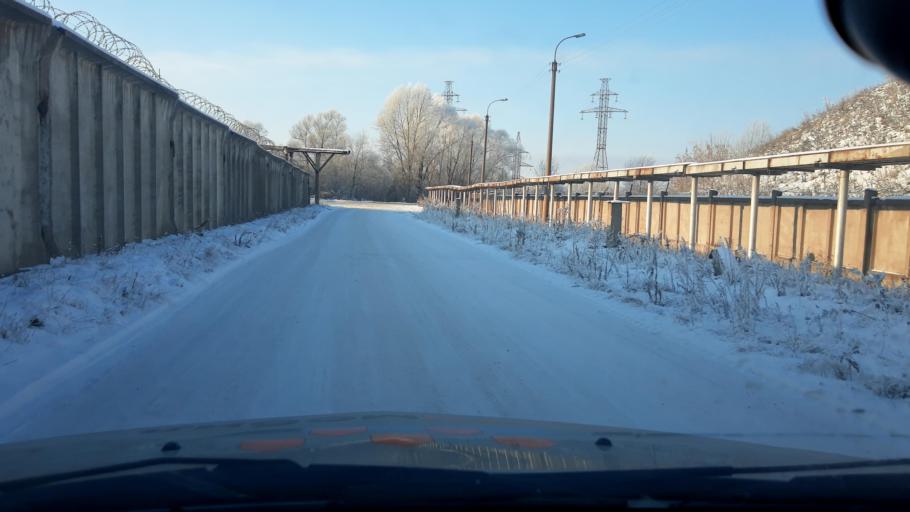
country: RU
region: Bashkortostan
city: Ufa
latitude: 54.8339
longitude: 56.0660
